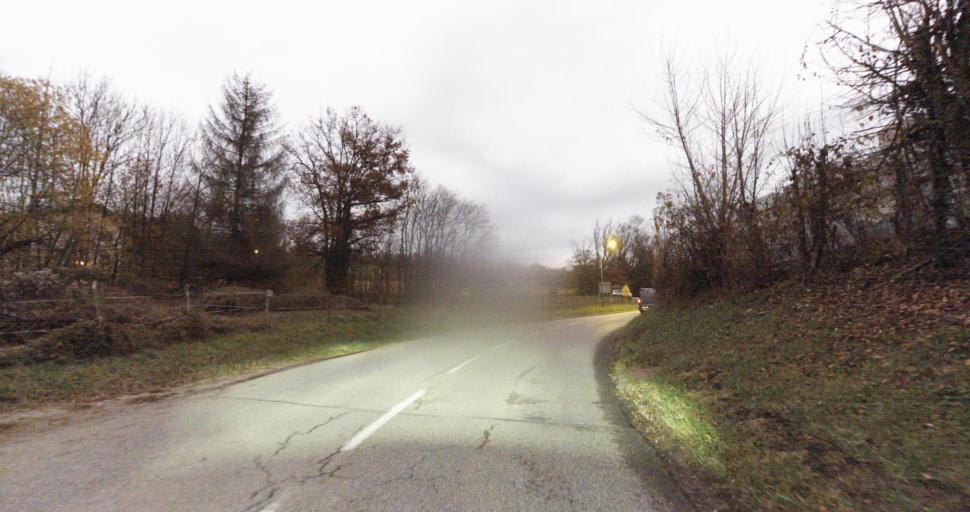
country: FR
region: Rhone-Alpes
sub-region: Departement de la Haute-Savoie
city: Alby-sur-Cheran
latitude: 45.8213
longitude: 6.0334
